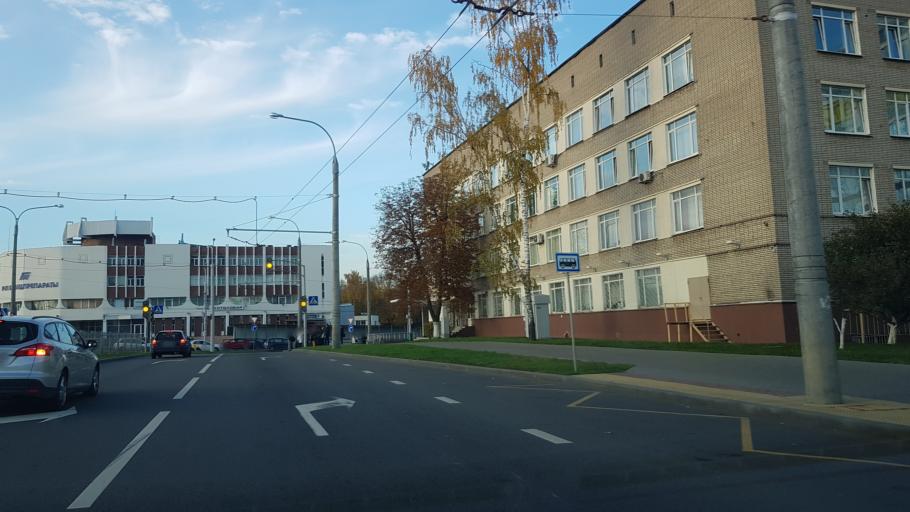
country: BY
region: Minsk
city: Minsk
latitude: 53.8849
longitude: 27.5683
